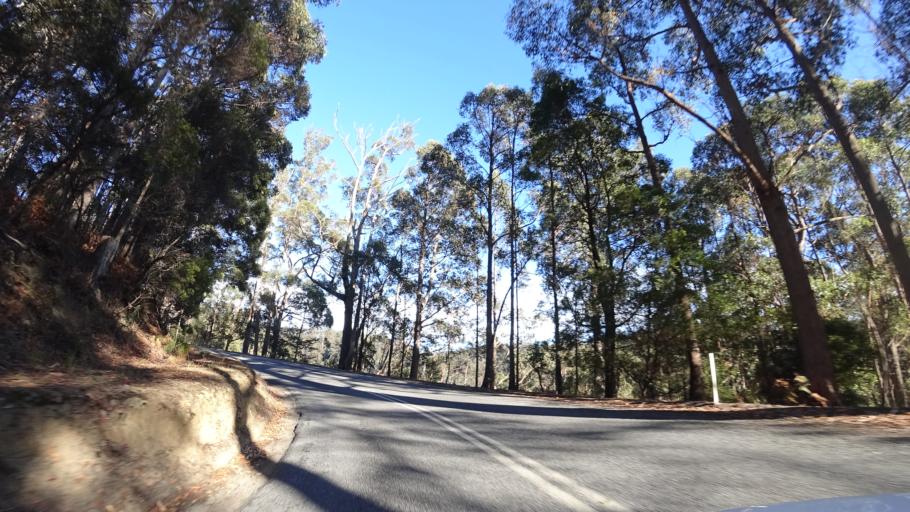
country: AU
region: Tasmania
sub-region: Break O'Day
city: St Helens
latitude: -41.2605
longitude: 148.0377
